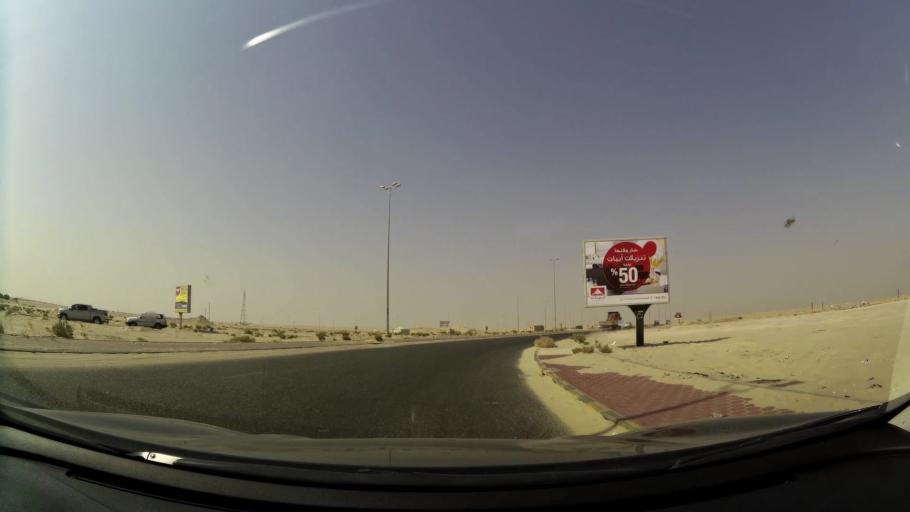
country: KW
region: Al Ahmadi
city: Al Wafrah
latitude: 28.8044
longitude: 48.0433
